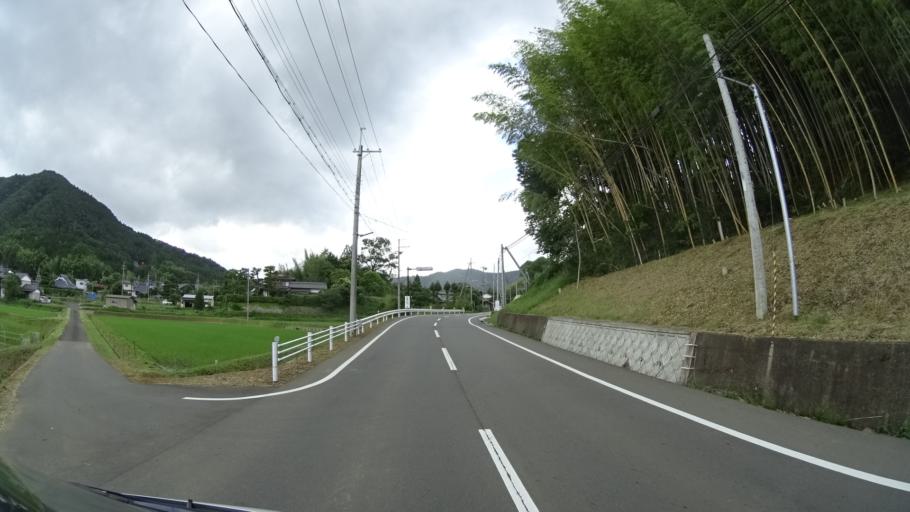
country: JP
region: Kyoto
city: Ayabe
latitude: 35.3401
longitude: 135.2021
